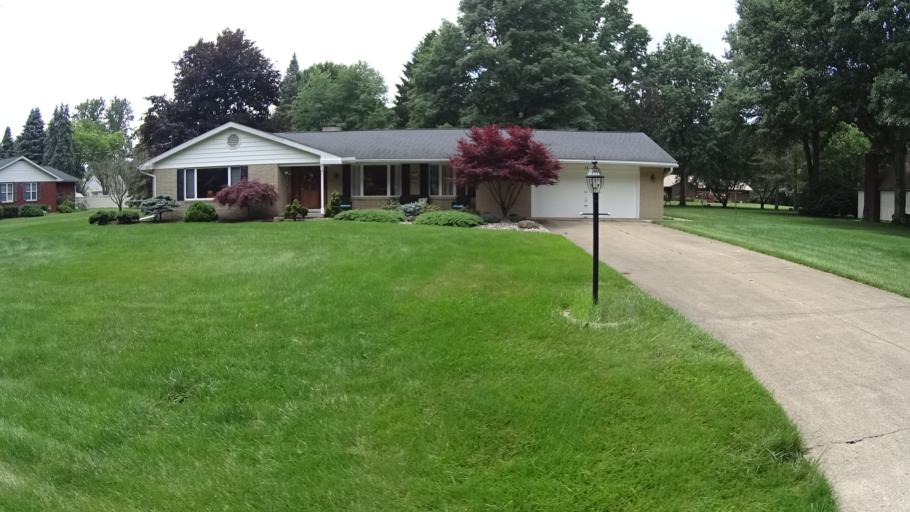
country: US
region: Ohio
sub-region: Erie County
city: Milan
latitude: 41.2903
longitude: -82.5943
